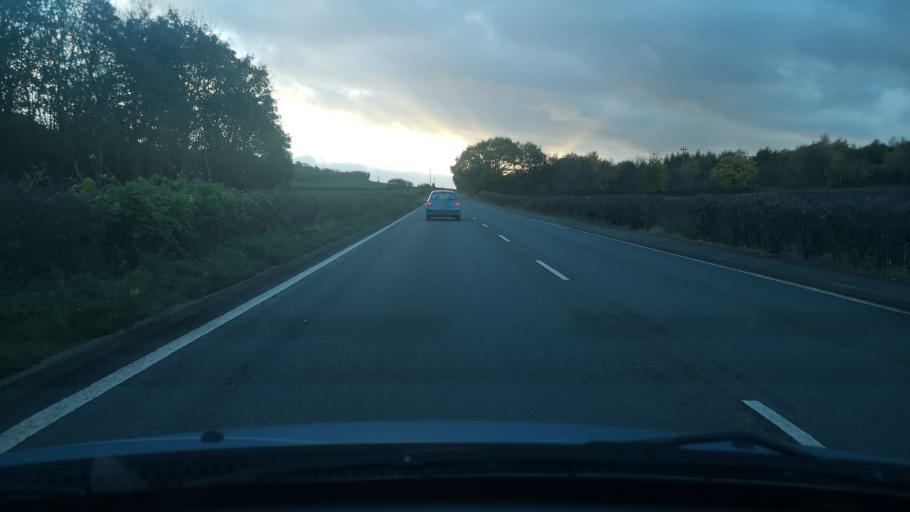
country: GB
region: England
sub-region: City and Borough of Wakefield
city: Horbury
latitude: 53.6307
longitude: -1.5643
